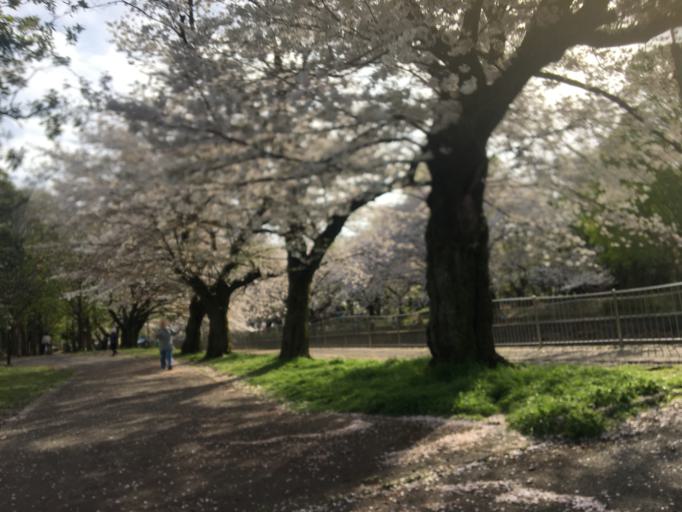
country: JP
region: Tokyo
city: Tokyo
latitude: 35.6934
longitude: 139.6342
